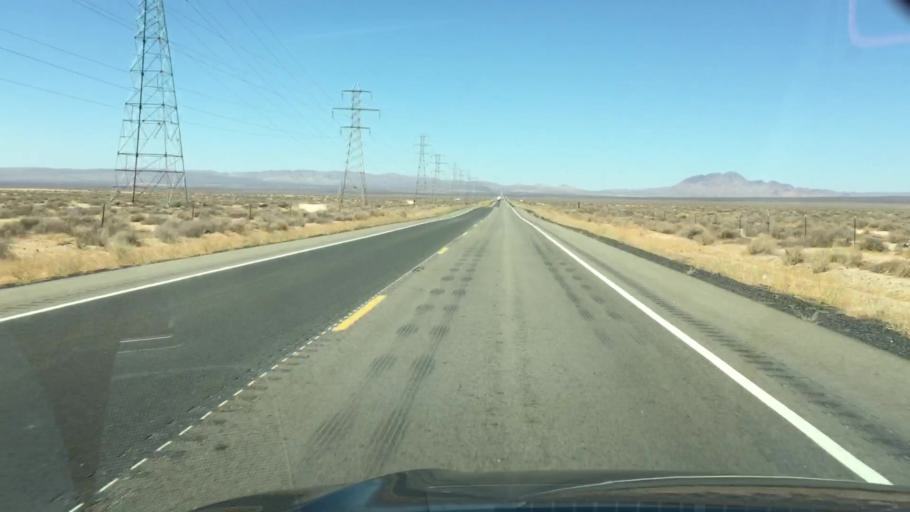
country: US
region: California
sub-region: Kern County
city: Boron
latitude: 35.1504
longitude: -117.5855
